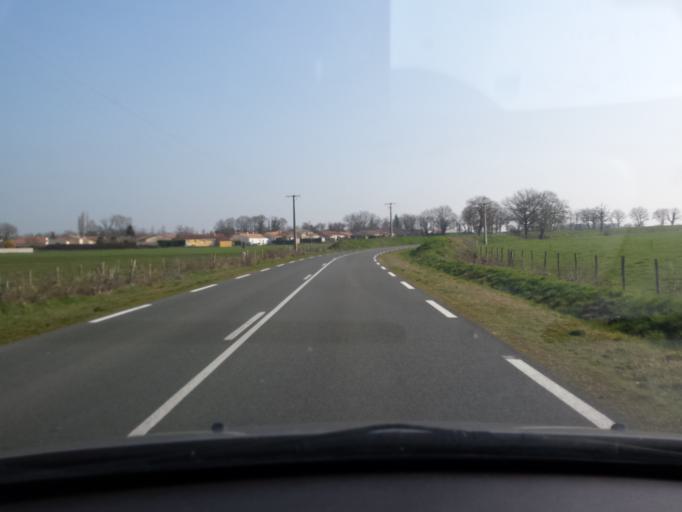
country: FR
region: Pays de la Loire
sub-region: Departement de la Vendee
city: La Ferriere
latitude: 46.7068
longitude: -1.3147
